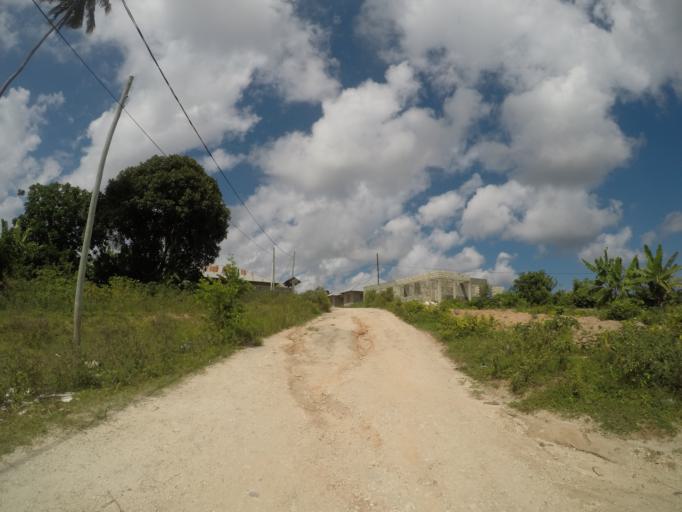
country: TZ
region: Pemba South
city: Chake Chake
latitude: -5.2325
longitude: 39.7803
